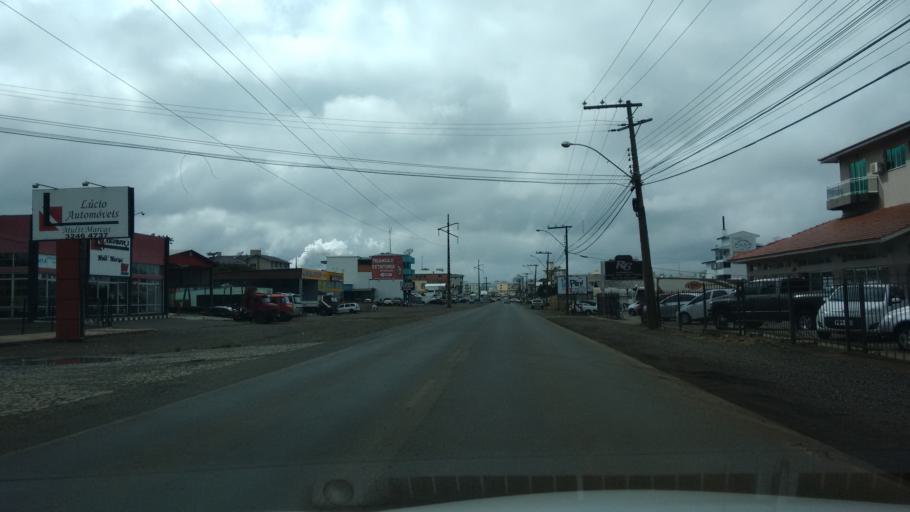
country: BR
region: Santa Catarina
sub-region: Videira
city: Videira
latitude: -27.0199
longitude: -50.9315
